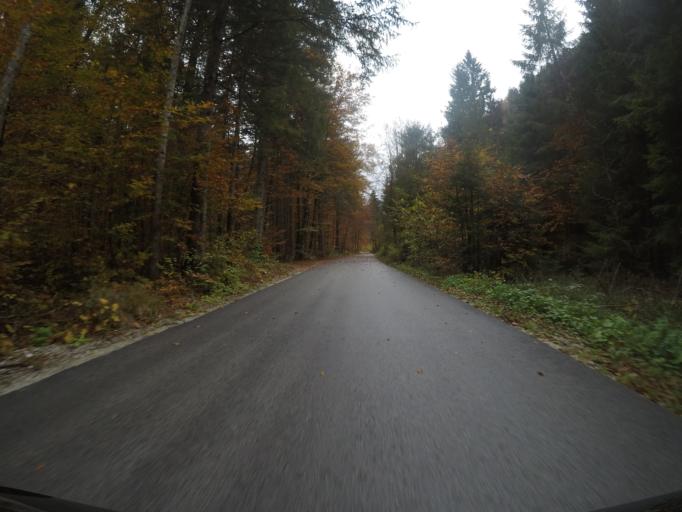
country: SI
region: Jesenice
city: Hrusica
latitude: 46.4283
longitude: 13.9688
